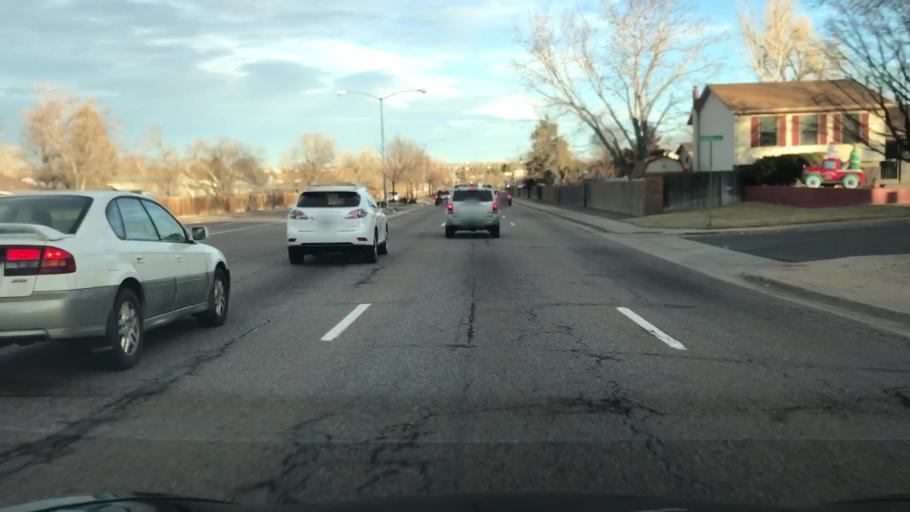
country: US
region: Colorado
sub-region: Adams County
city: Aurora
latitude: 39.6736
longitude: -104.7990
